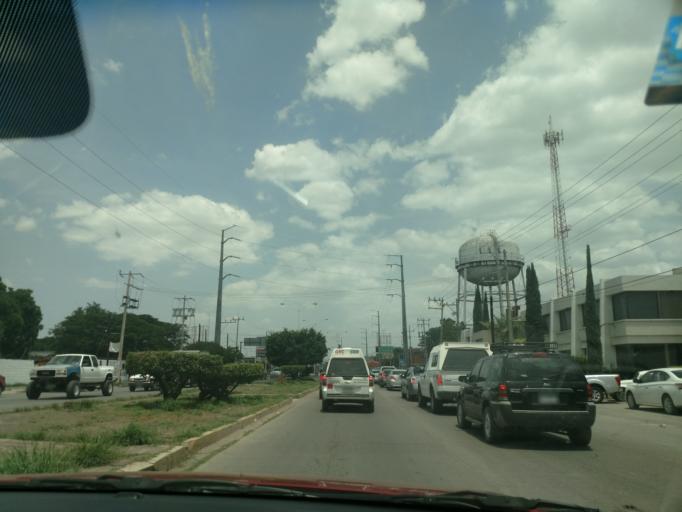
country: MX
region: San Luis Potosi
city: Rio Verde
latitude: 21.9254
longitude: -100.0020
